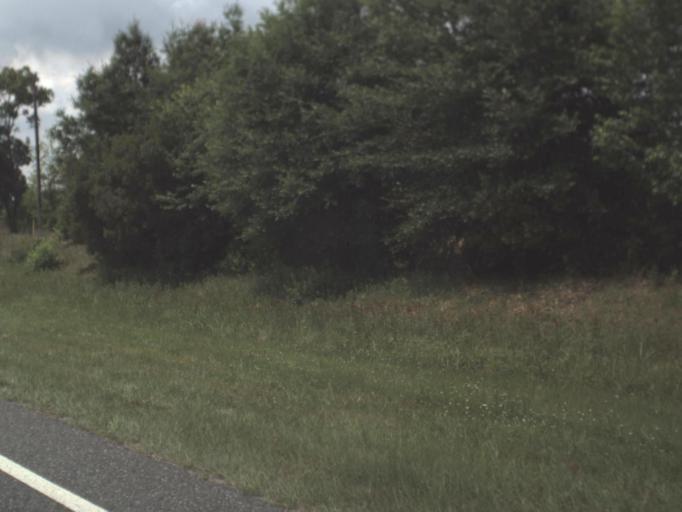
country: US
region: Florida
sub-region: Putnam County
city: East Palatka
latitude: 29.7726
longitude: -81.6390
